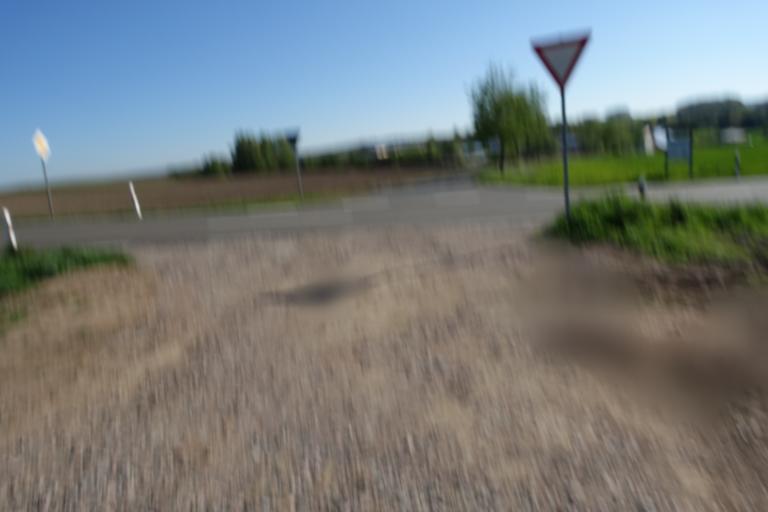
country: DE
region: Saxony
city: Niederschona
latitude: 50.9019
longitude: 13.4261
